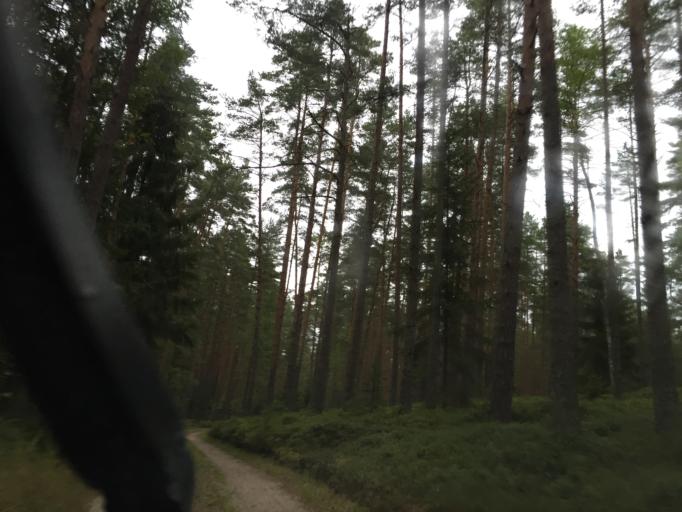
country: LV
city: Tireli
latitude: 56.8401
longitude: 23.6179
